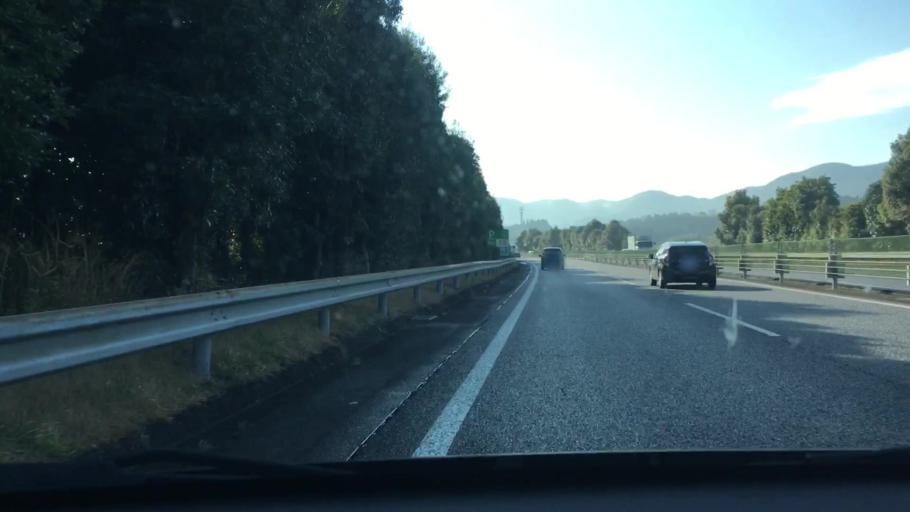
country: JP
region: Kagoshima
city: Okuchi-shinohara
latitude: 32.0154
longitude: 130.7636
